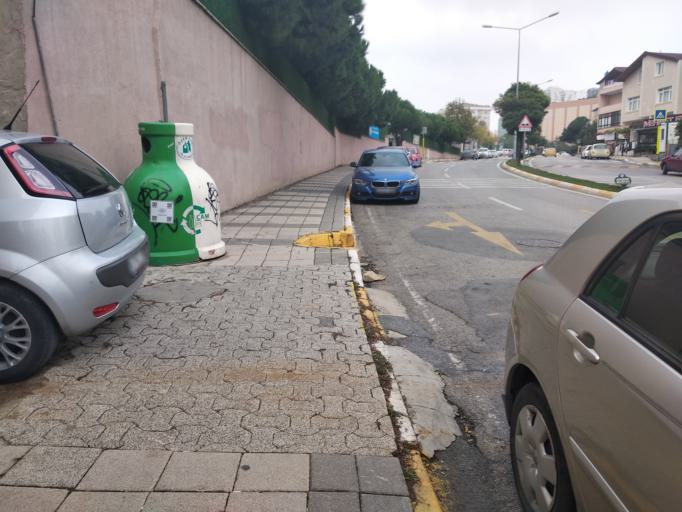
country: TR
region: Istanbul
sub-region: Atasehir
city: Atasehir
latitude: 40.9842
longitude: 29.1154
